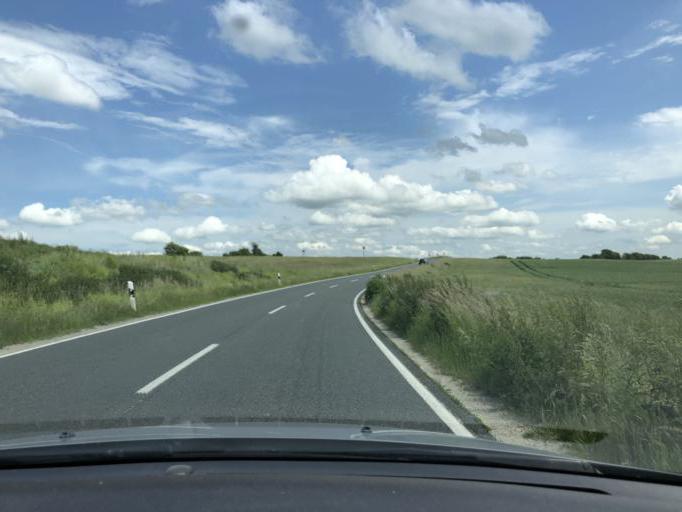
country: DE
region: Thuringia
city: Wachstedt
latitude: 51.2953
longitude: 10.2551
